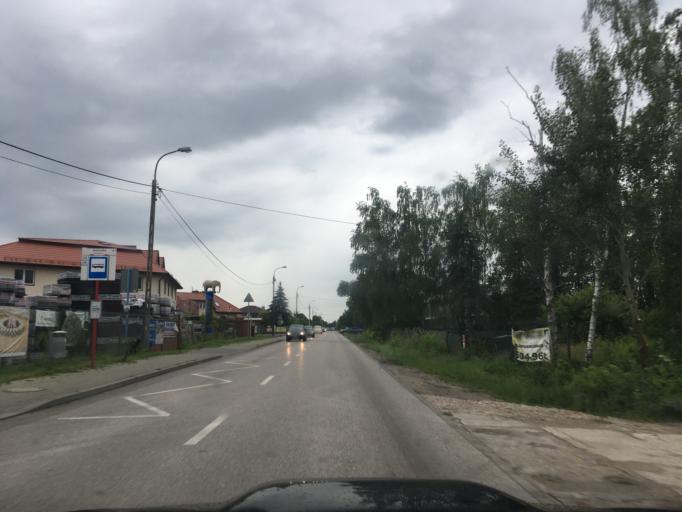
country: PL
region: Masovian Voivodeship
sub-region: Powiat piaseczynski
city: Zalesie Gorne
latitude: 52.0392
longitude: 21.0125
